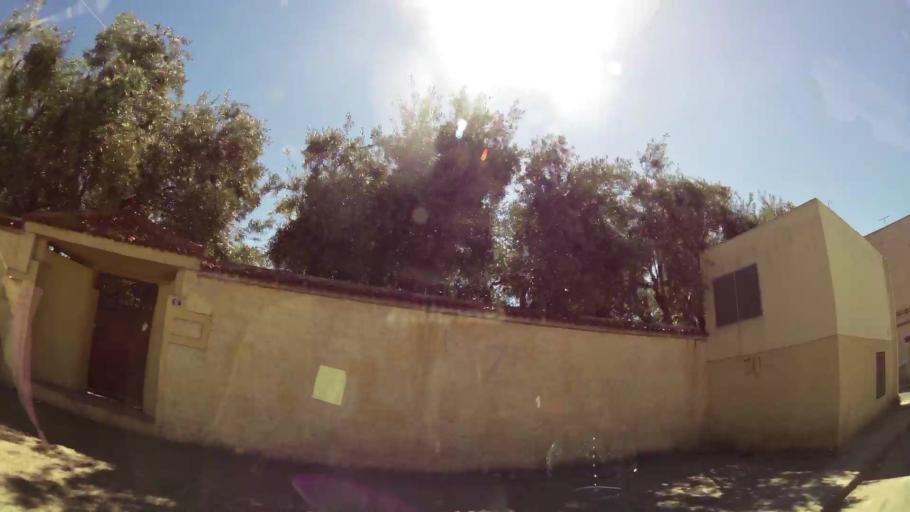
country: MA
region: Fes-Boulemane
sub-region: Fes
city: Fes
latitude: 34.0204
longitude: -4.9932
